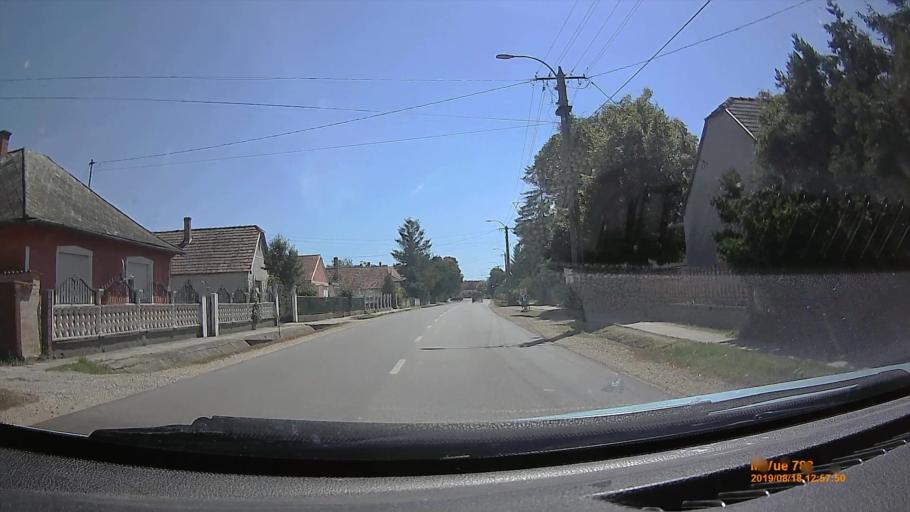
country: HU
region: Fejer
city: Sarkeresztur
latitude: 47.0100
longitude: 18.5457
